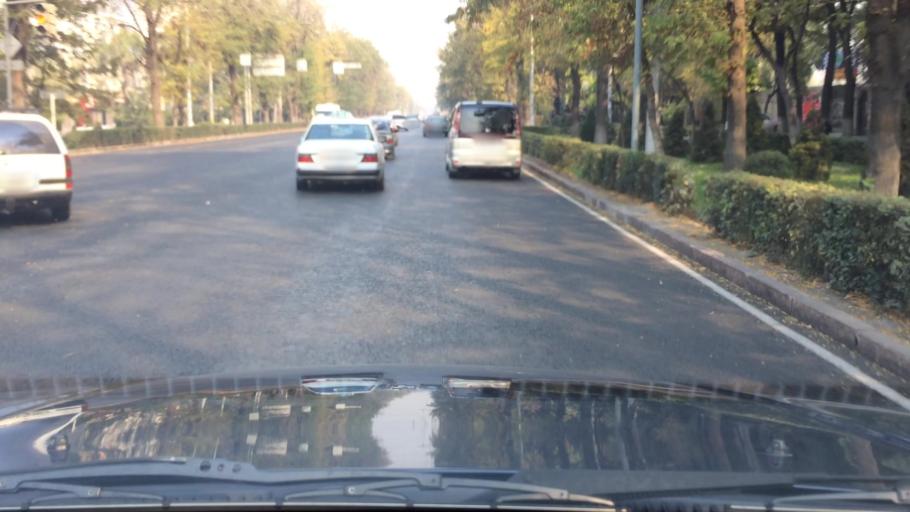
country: KG
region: Chuy
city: Bishkek
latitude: 42.8508
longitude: 74.5865
